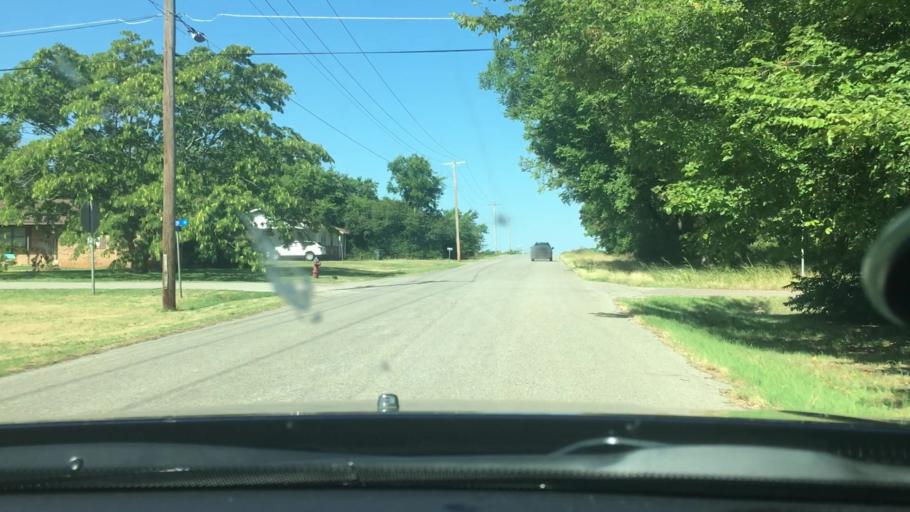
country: US
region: Oklahoma
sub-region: Marshall County
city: Madill
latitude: 34.0965
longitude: -96.7630
